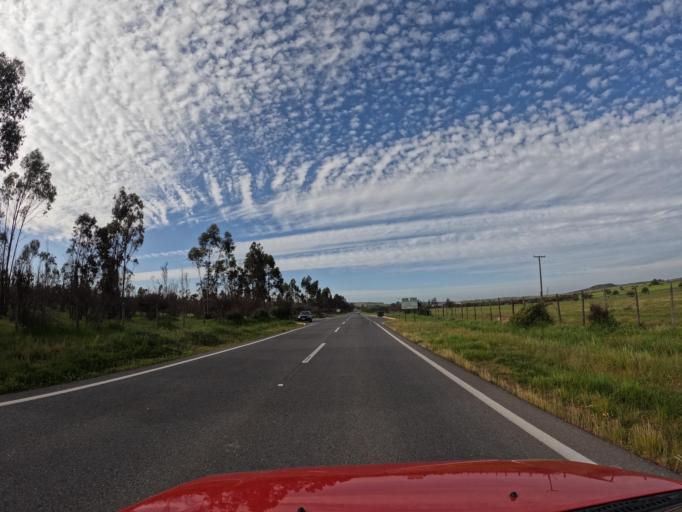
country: CL
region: O'Higgins
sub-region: Provincia de Colchagua
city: Santa Cruz
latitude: -34.2335
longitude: -71.7280
